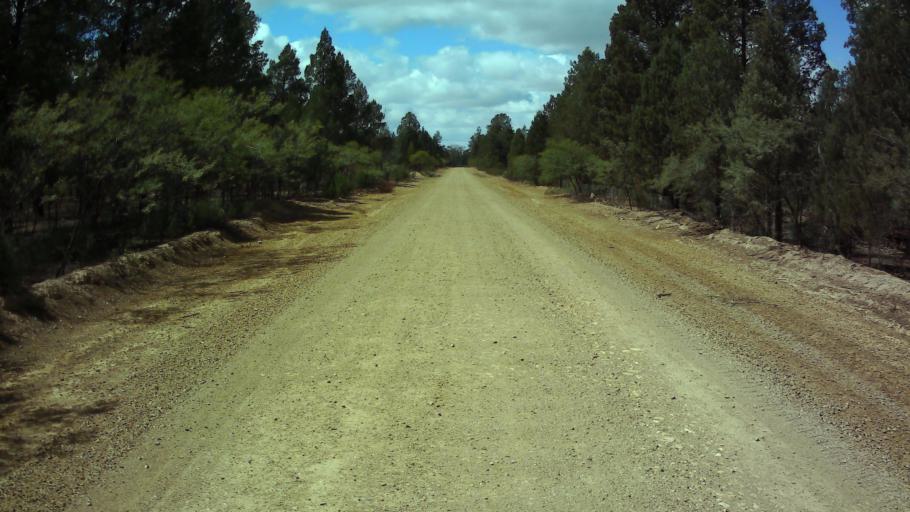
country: AU
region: New South Wales
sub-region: Weddin
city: Grenfell
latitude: -33.9105
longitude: 147.9196
